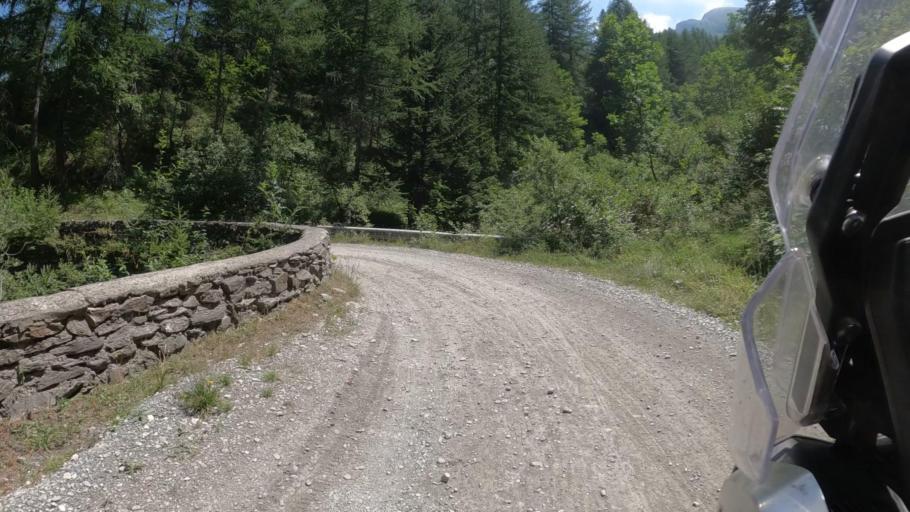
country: IT
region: Piedmont
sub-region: Provincia di Torino
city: Meana di Susa
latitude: 45.0910
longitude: 7.0602
